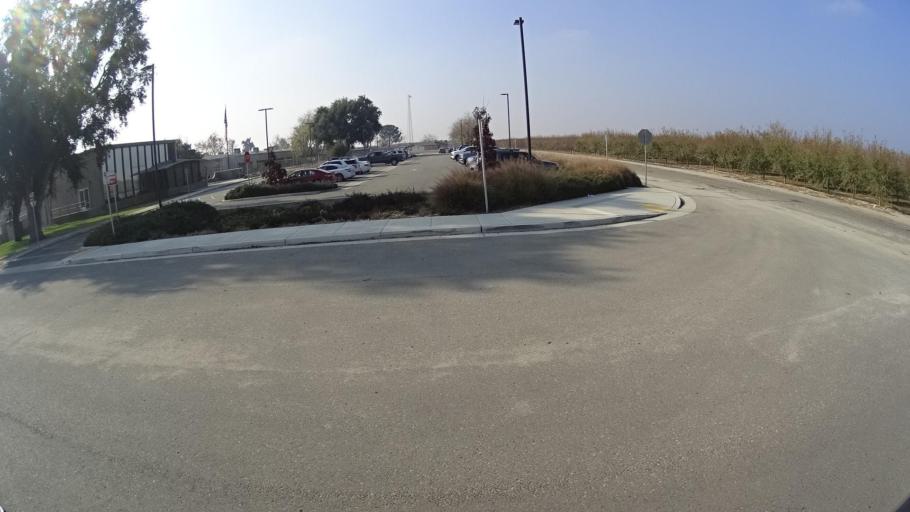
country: US
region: California
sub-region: Kern County
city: Greenfield
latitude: 35.2233
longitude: -119.1100
